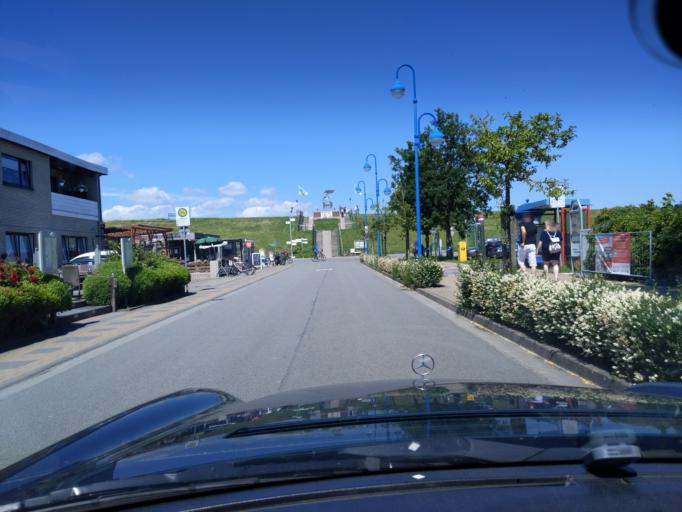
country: DE
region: Lower Saxony
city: Butjadingen
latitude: 53.5778
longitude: 8.2472
